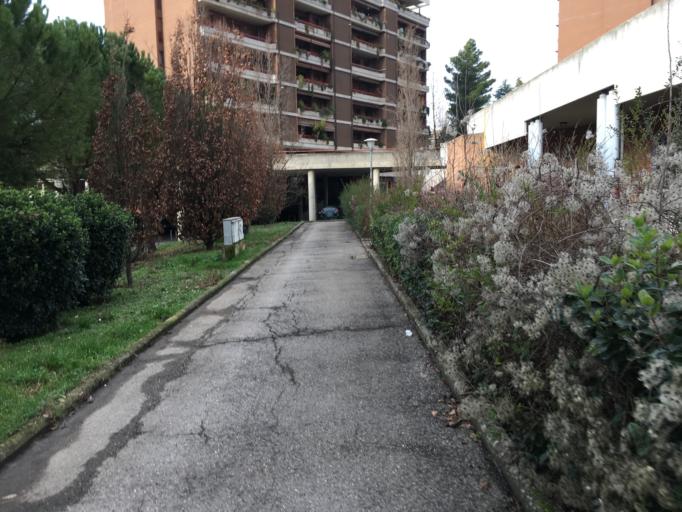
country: IT
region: Umbria
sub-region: Provincia di Perugia
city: Perugia
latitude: 43.0997
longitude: 12.3710
